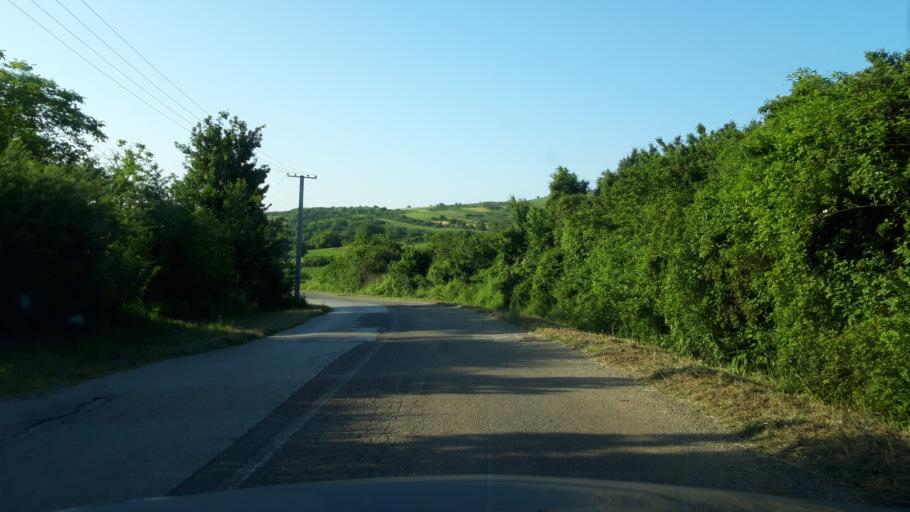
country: RS
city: Glozan
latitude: 45.1658
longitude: 19.5883
